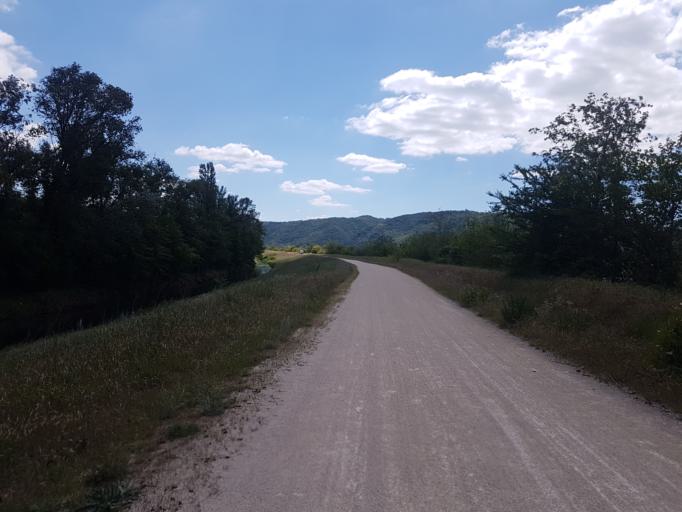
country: FR
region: Rhone-Alpes
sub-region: Departement de l'Ardeche
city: Mauves
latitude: 45.0366
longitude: 4.8439
